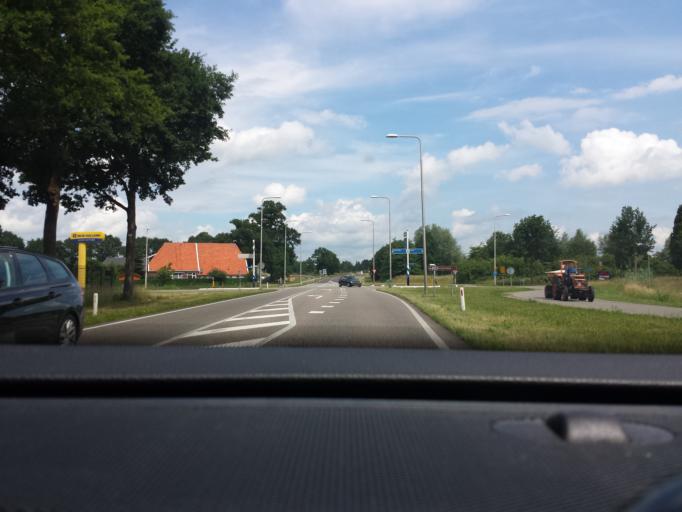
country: NL
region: Gelderland
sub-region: Berkelland
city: Neede
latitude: 52.1340
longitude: 6.5923
